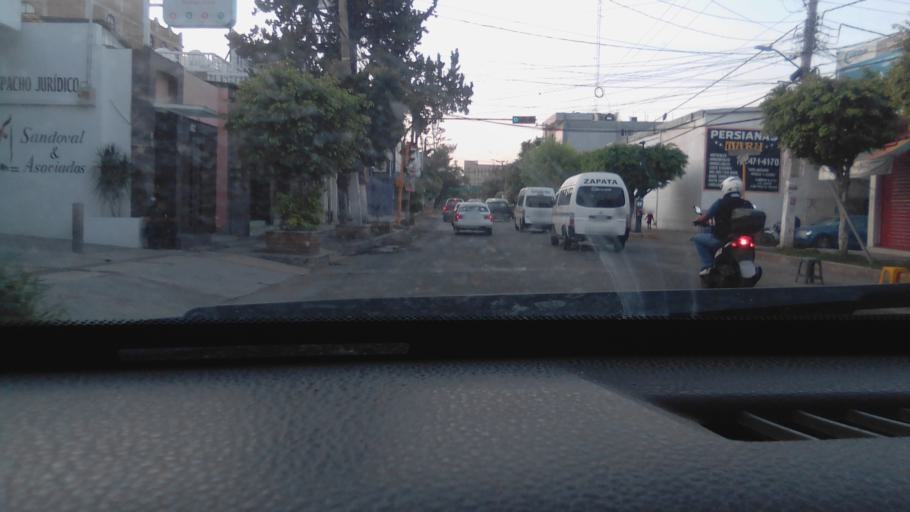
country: MX
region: Guerrero
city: Chilpancingo de los Bravos
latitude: 17.5576
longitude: -99.5054
